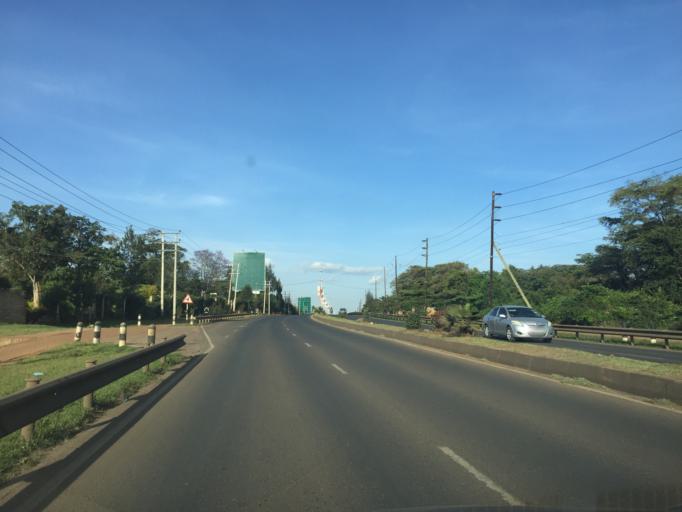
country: KE
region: Nairobi Area
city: Nairobi
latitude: -1.3364
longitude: 36.7756
